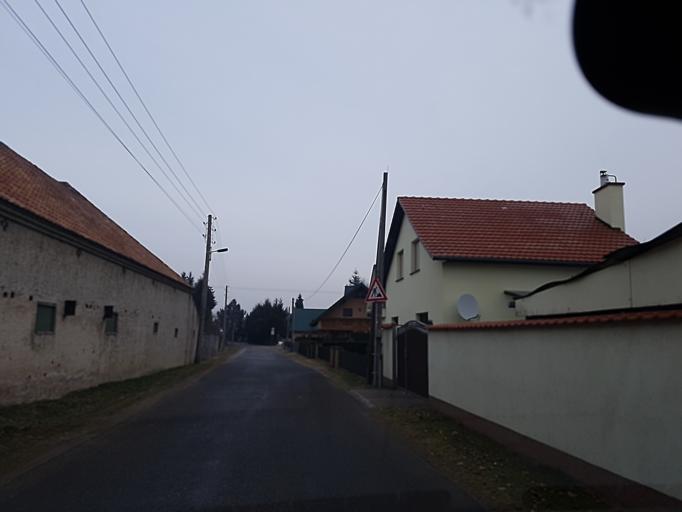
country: DE
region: Brandenburg
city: Ruckersdorf
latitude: 51.5647
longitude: 13.5454
